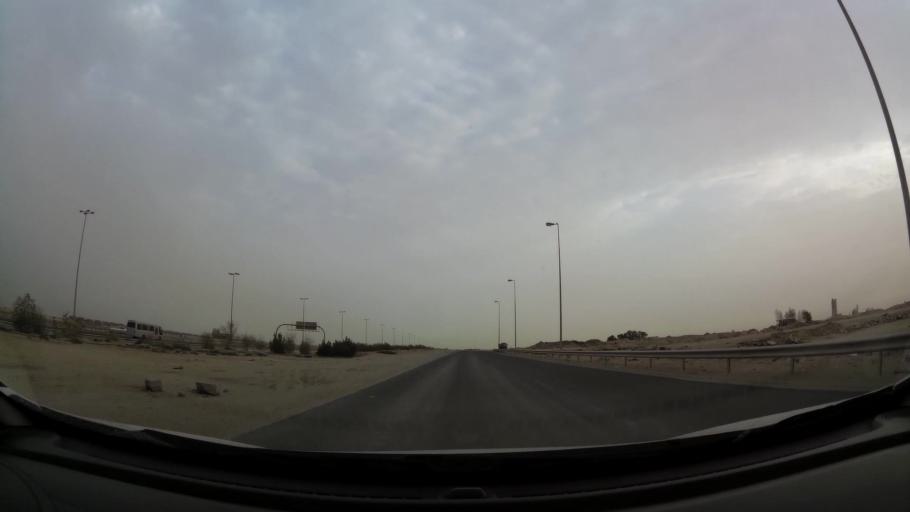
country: BH
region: Northern
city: Ar Rifa'
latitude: 26.0417
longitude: 50.6070
